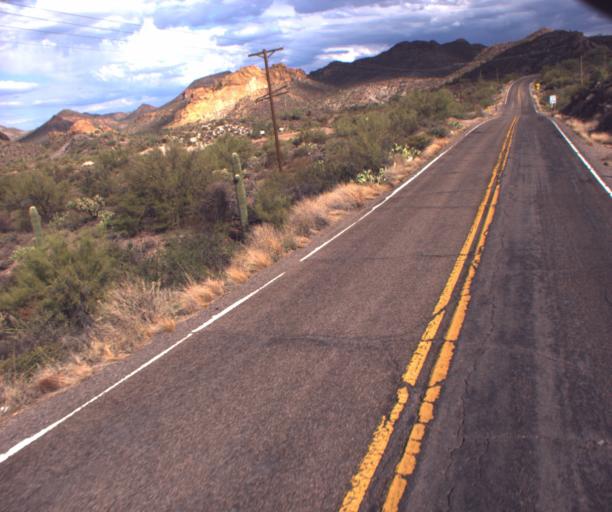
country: US
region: Arizona
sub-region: Pinal County
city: Apache Junction
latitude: 33.4996
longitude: -111.4627
